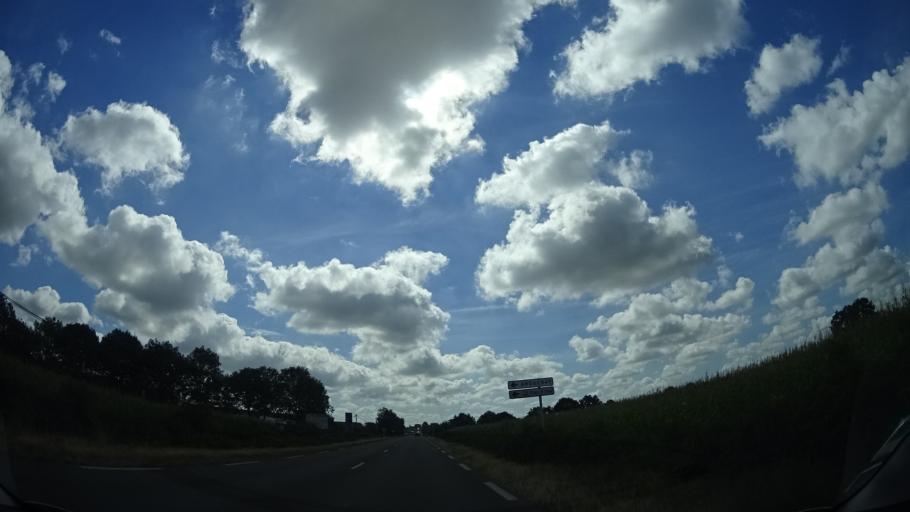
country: FR
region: Pays de la Loire
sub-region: Departement de la Mayenne
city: Meslay-du-Maine
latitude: 47.9681
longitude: -0.5864
